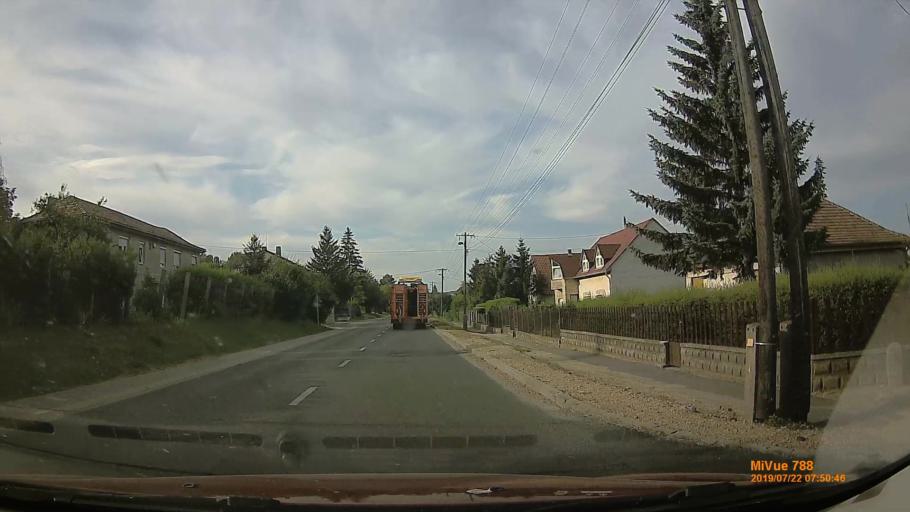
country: HU
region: Veszprem
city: Ajka
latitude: 47.0629
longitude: 17.5529
